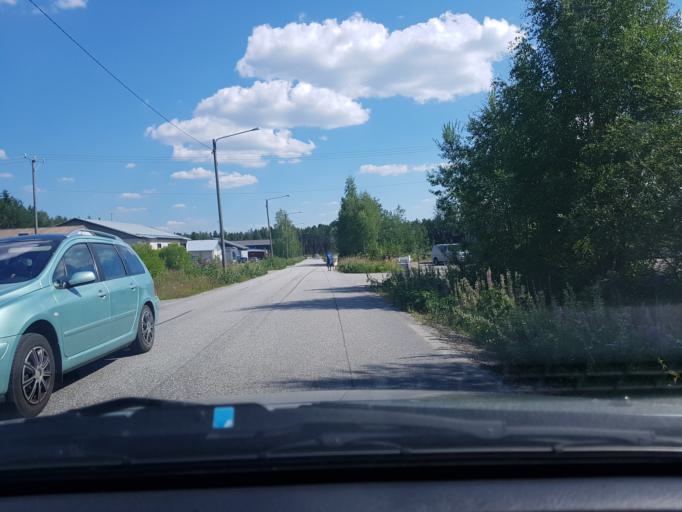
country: FI
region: Kainuu
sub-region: Kehys-Kainuu
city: Kuhmo
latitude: 64.1296
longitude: 29.4793
